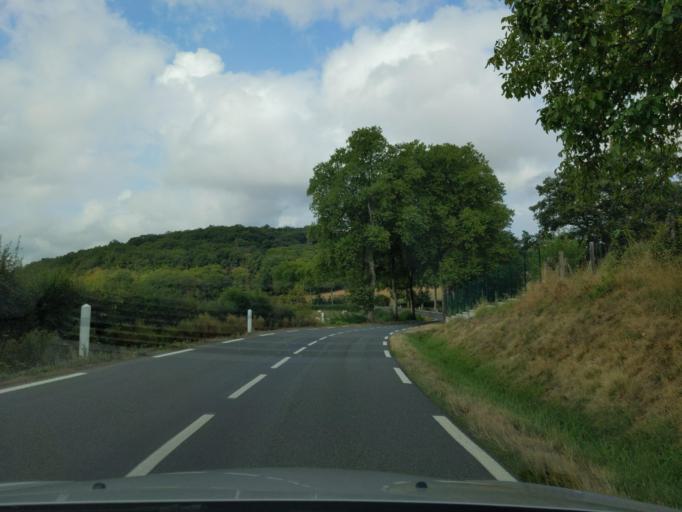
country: FR
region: Bourgogne
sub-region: Departement de la Nievre
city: Luzy
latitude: 46.7678
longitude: 3.9489
